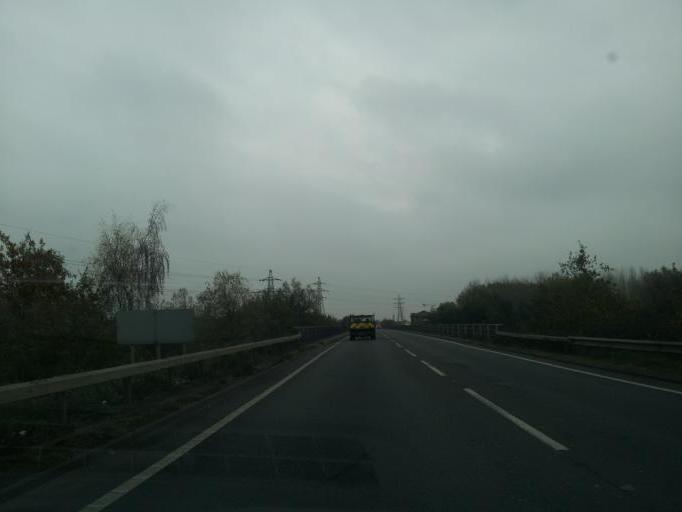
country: GB
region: England
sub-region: Bedford
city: Little Barford
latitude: 52.2084
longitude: -0.2781
